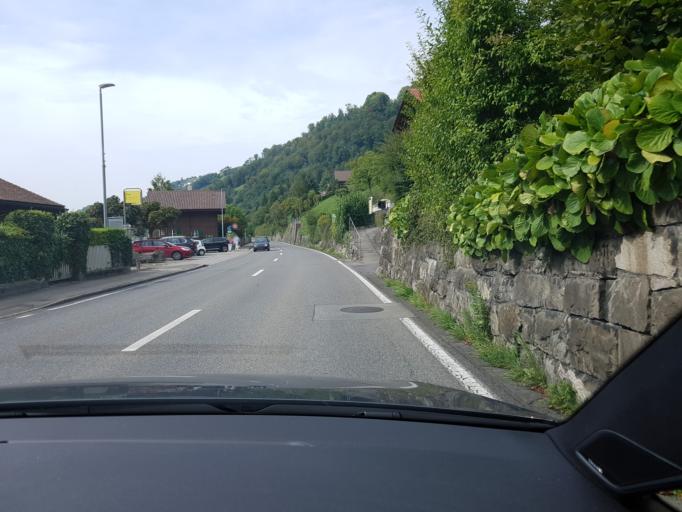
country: CH
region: Bern
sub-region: Thun District
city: Sigriswil
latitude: 46.7039
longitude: 7.7301
